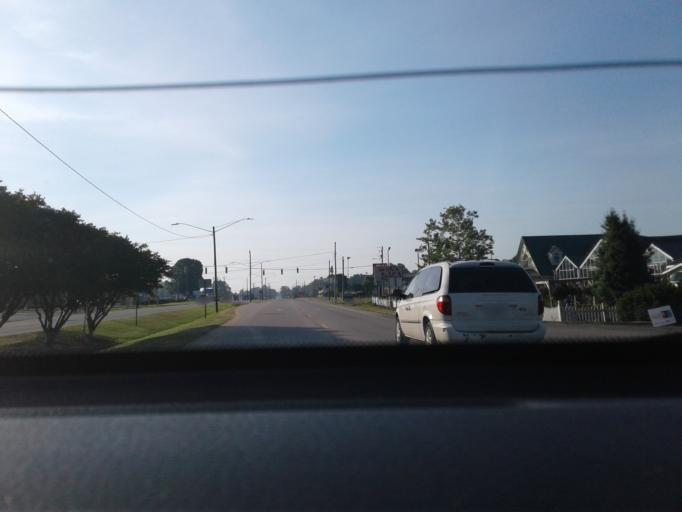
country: US
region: North Carolina
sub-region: Harnett County
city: Dunn
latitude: 35.3176
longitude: -78.6288
